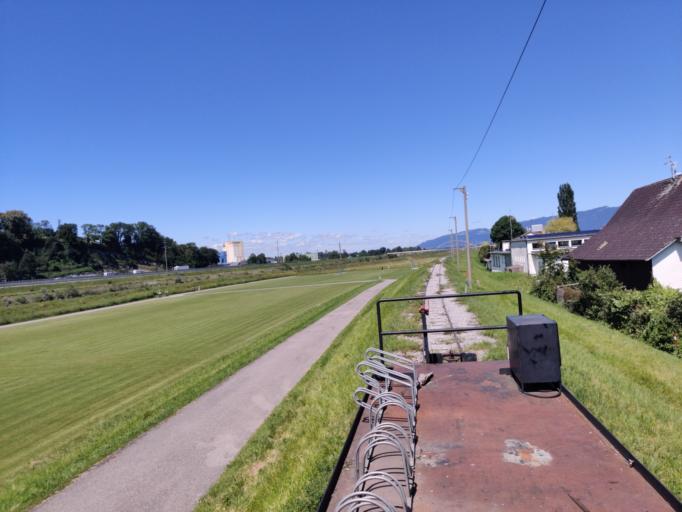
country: CH
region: Saint Gallen
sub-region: Wahlkreis Rheintal
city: Au
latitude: 47.4383
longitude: 9.6472
